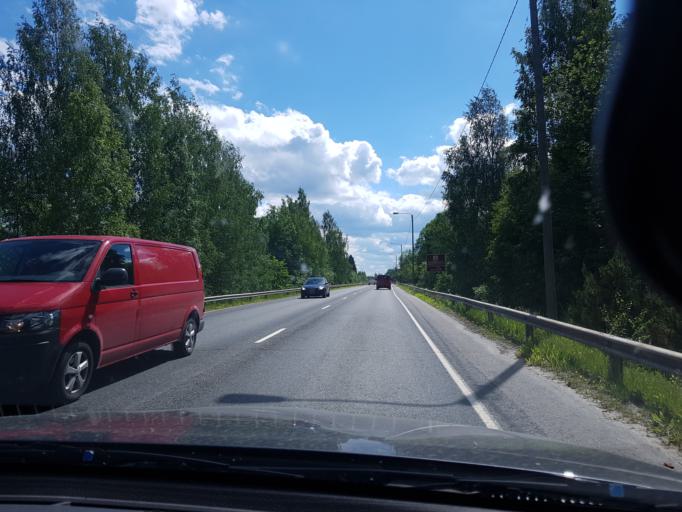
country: FI
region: Haeme
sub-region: Haemeenlinna
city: Parola
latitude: 61.0651
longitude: 24.3924
